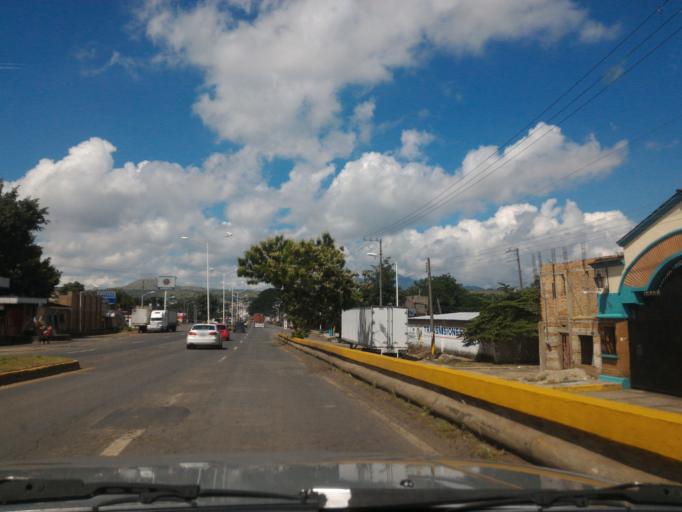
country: MX
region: Jalisco
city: Tequila
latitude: 20.8794
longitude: -103.8242
